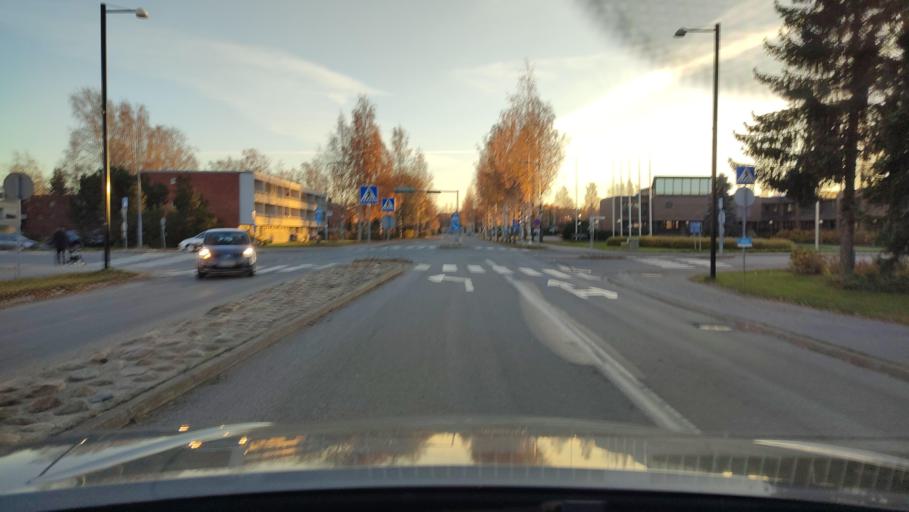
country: FI
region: Ostrobothnia
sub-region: Sydosterbotten
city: Naerpes
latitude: 62.4732
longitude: 21.3374
